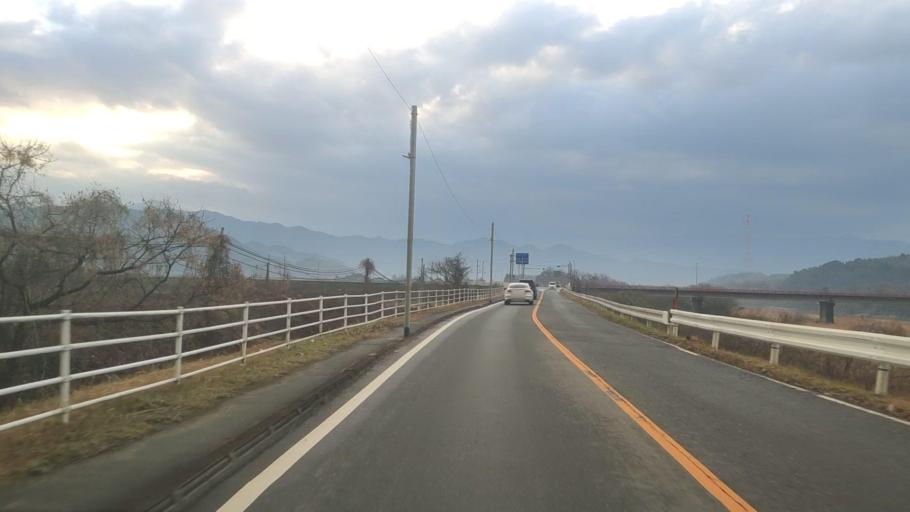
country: JP
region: Kumamoto
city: Uto
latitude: 32.6946
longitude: 130.7890
